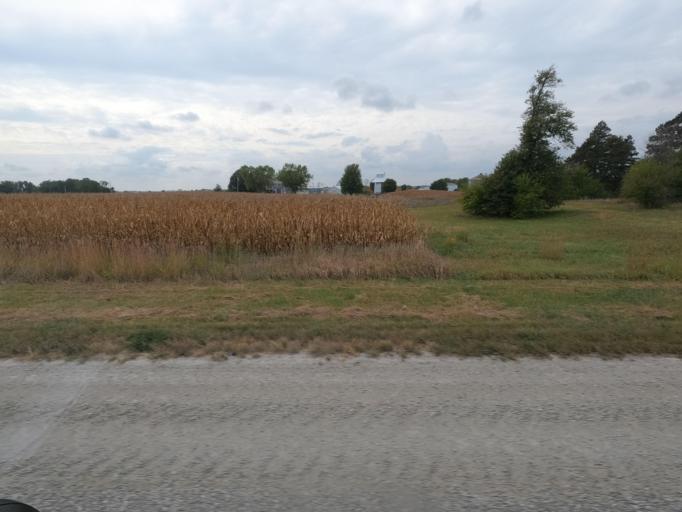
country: US
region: Iowa
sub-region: Jasper County
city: Monroe
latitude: 41.5037
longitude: -93.0815
